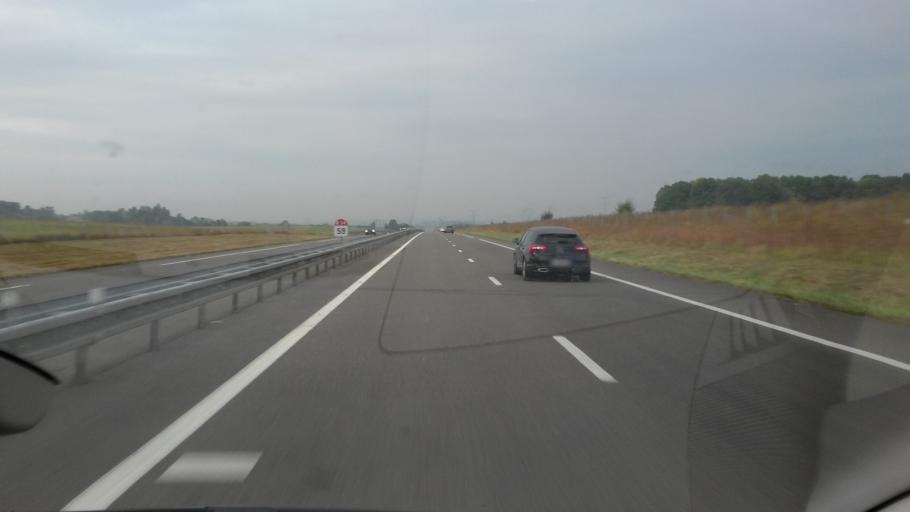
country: FR
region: Champagne-Ardenne
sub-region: Departement des Ardennes
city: Rethel
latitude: 49.5839
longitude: 4.4877
